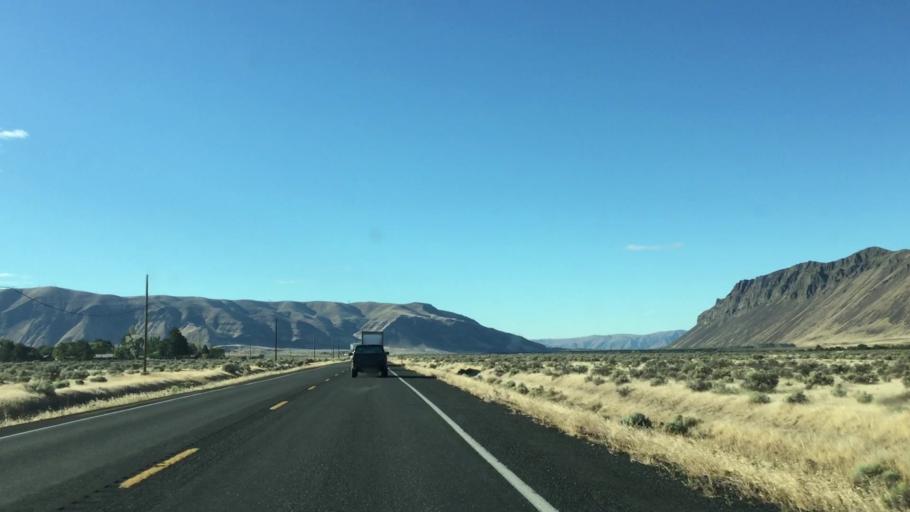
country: US
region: Washington
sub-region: Grant County
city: Mattawa
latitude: 46.8655
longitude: -119.9532
